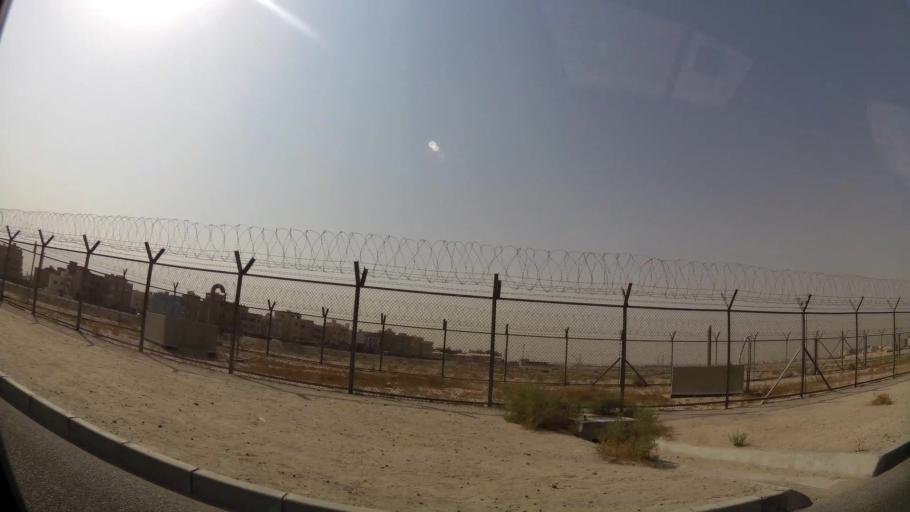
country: KW
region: Muhafazat al Jahra'
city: Al Jahra'
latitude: 29.3338
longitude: 47.7736
